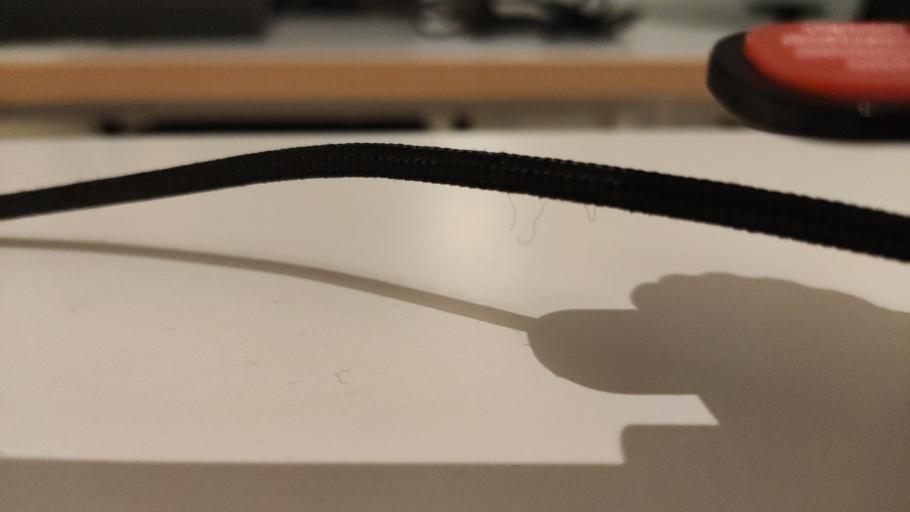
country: RU
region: Moskovskaya
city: Zhilevo
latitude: 55.0999
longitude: 38.0530
